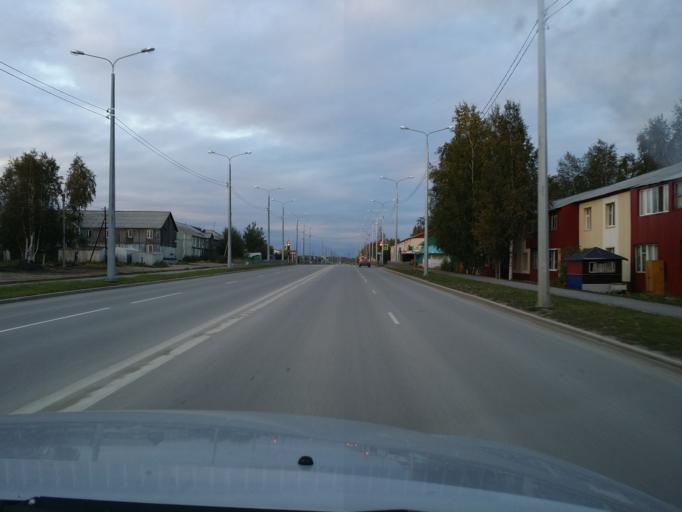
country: RU
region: Khanty-Mansiyskiy Avtonomnyy Okrug
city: Megion
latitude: 61.0359
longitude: 76.0952
